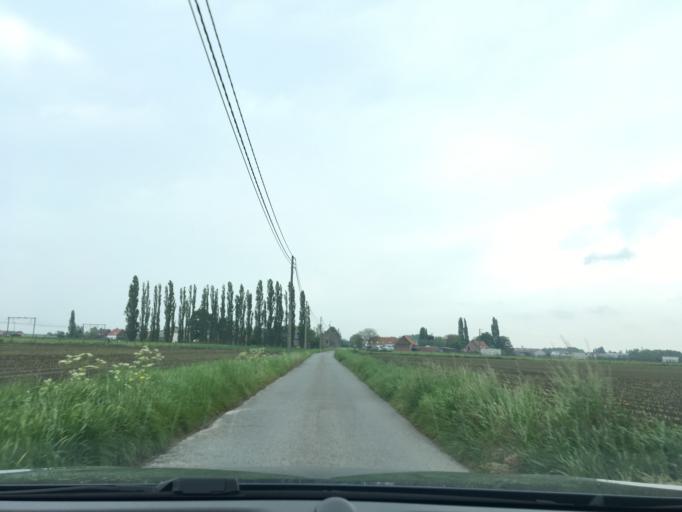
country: BE
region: Flanders
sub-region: Provincie West-Vlaanderen
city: Lichtervelde
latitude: 51.0090
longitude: 3.1252
